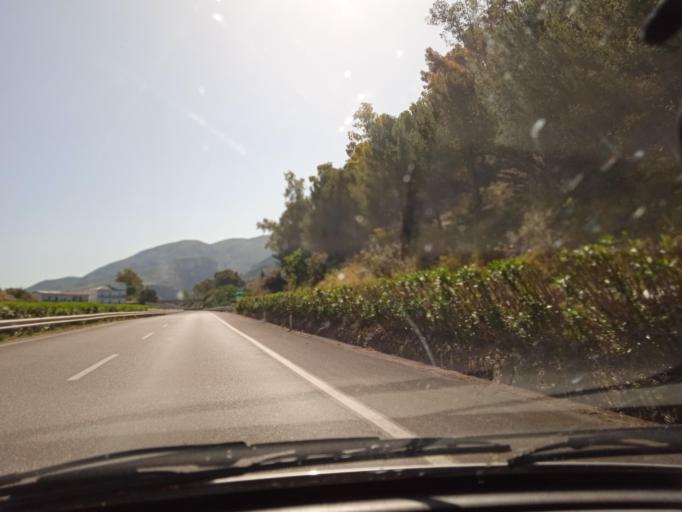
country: IT
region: Sicily
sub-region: Messina
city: Torrenova
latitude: 38.0810
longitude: 14.6747
